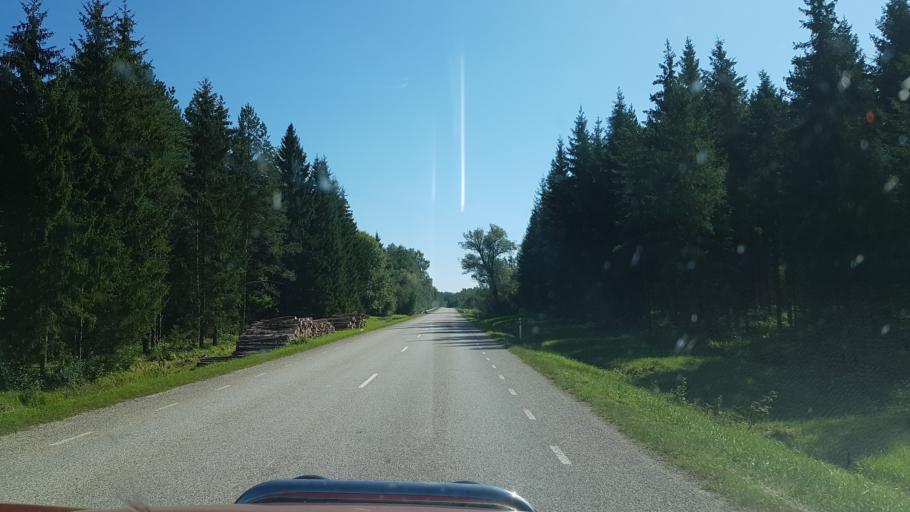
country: EE
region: Polvamaa
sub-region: Polva linn
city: Polva
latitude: 58.2670
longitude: 27.1565
